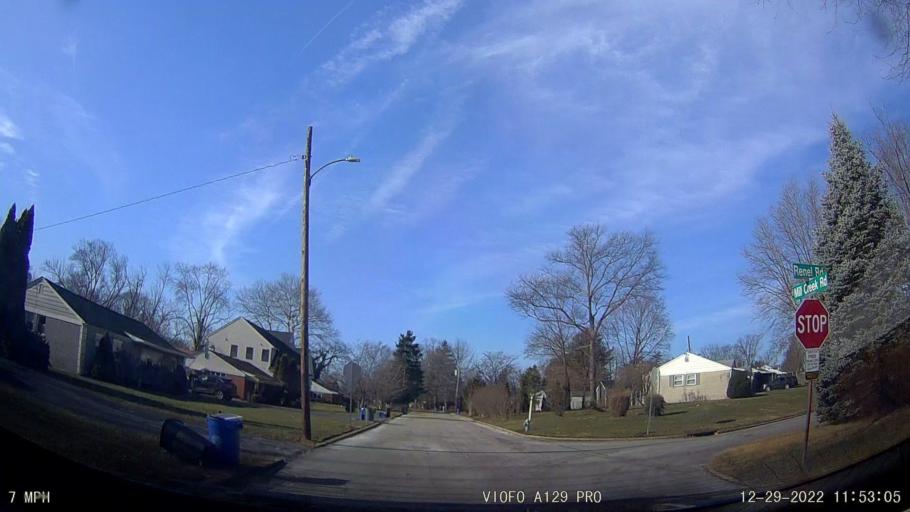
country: US
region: Pennsylvania
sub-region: Montgomery County
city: Norristown
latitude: 40.1319
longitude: -75.3040
